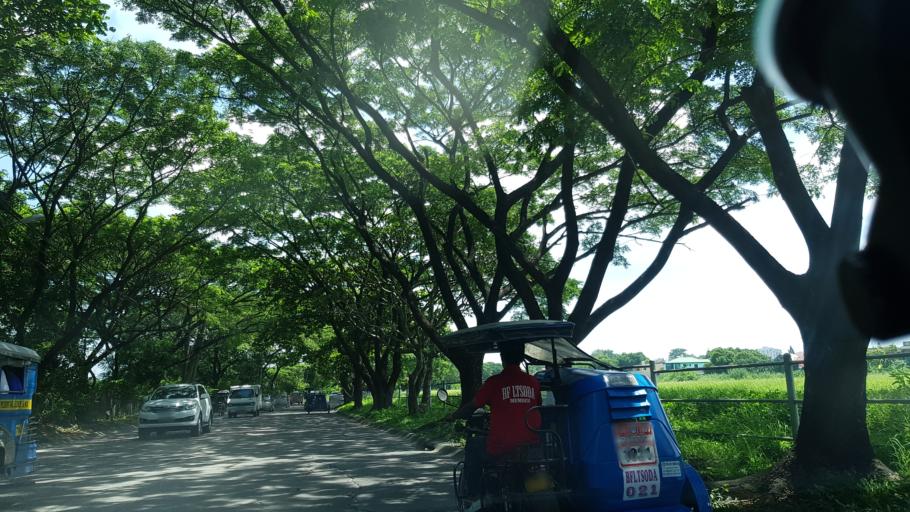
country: PH
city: Sambayanihan People's Village
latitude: 14.4474
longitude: 121.0101
